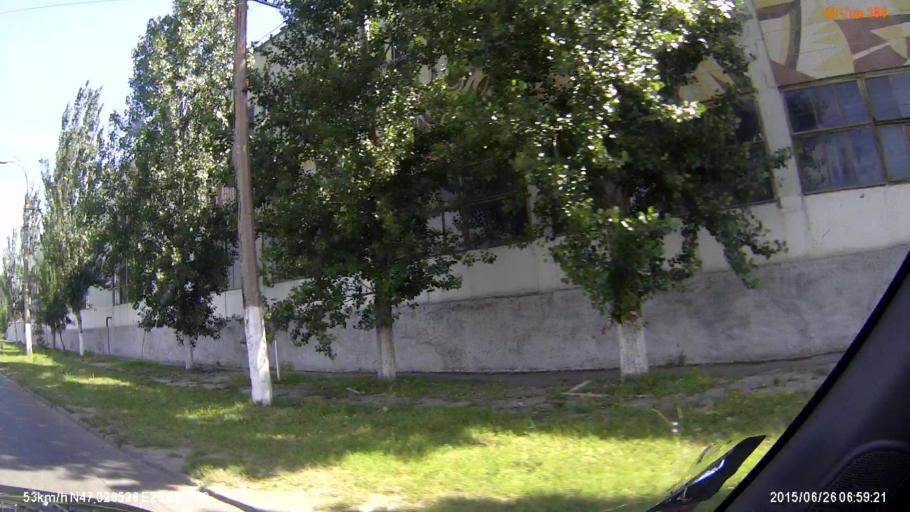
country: MD
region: Chisinau
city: Chisinau
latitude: 47.0264
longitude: 28.8654
